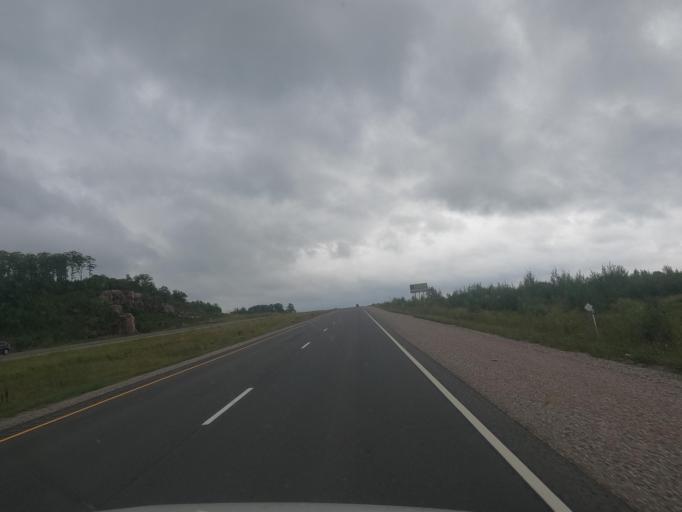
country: CA
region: Ontario
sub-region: Algoma
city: Sault Ste. Marie
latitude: 46.4632
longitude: -84.0592
